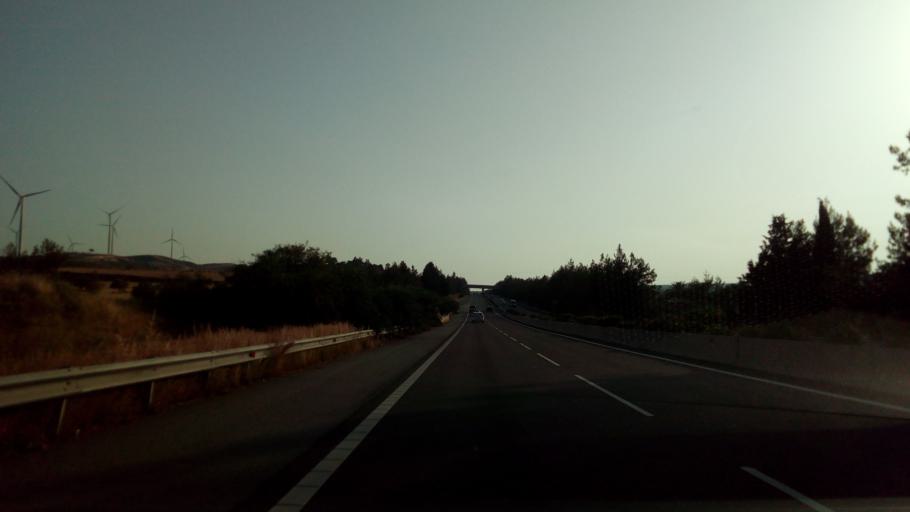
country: CY
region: Larnaka
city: Tersefanou
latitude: 34.8938
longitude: 33.5345
